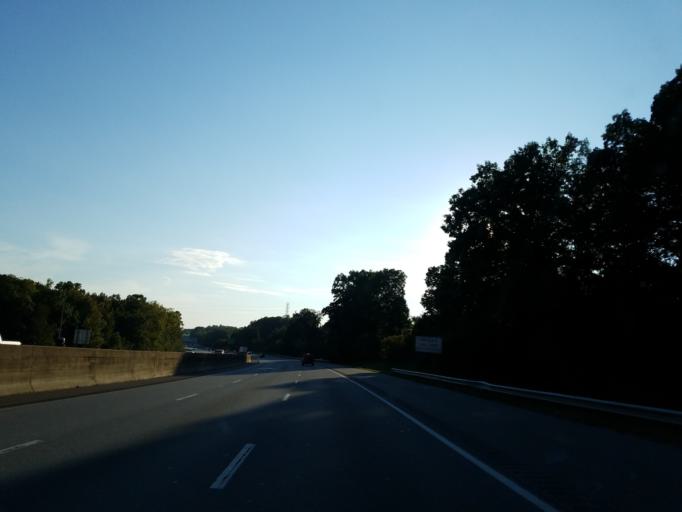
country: US
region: North Carolina
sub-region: Gaston County
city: Bessemer City
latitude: 35.2605
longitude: -81.2845
